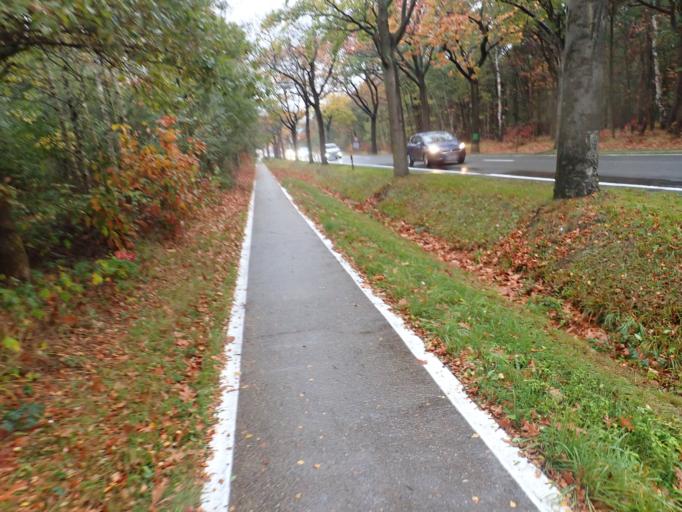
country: BE
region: Flanders
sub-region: Provincie Antwerpen
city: Wuustwezel
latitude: 51.3752
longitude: 4.6092
